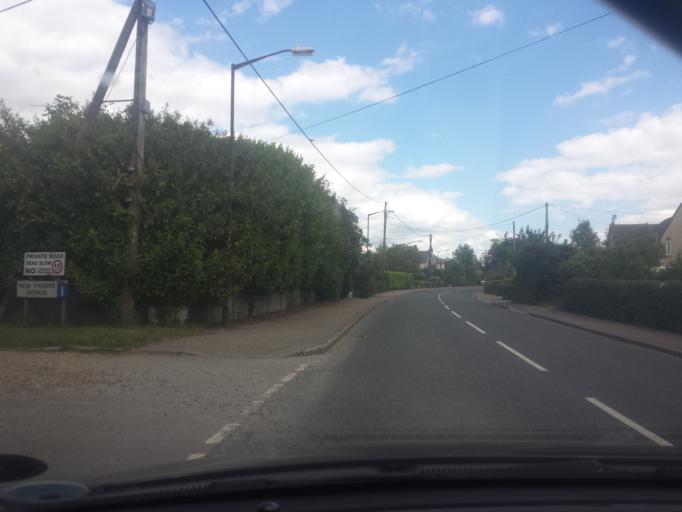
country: GB
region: England
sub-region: Essex
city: Little Clacton
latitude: 51.8583
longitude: 1.1667
